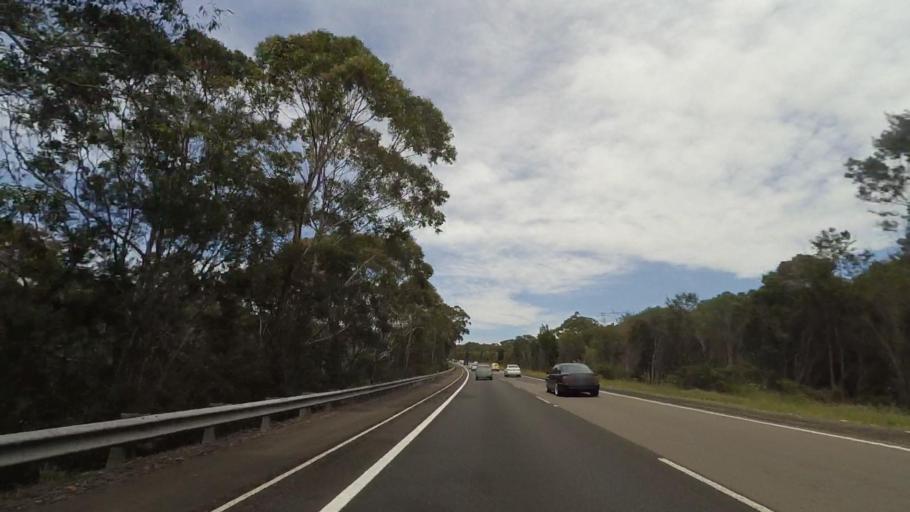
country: AU
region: New South Wales
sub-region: Wollongong
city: Helensburgh
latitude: -34.1642
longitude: 150.9798
